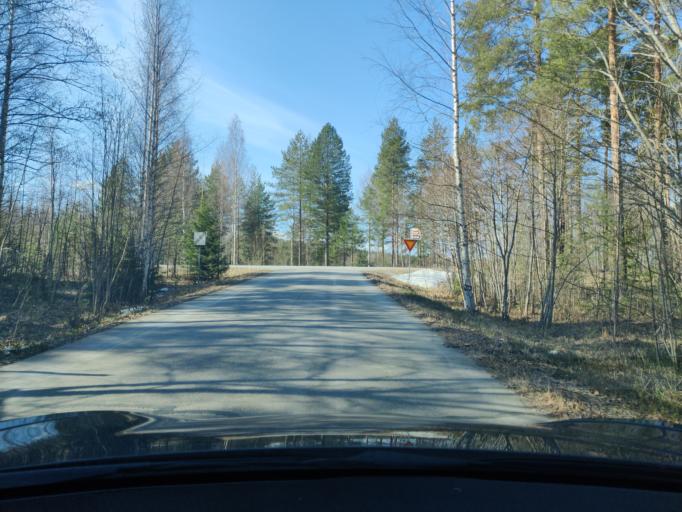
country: FI
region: Northern Savo
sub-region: Kuopio
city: Vehmersalmi
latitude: 62.7724
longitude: 27.9789
